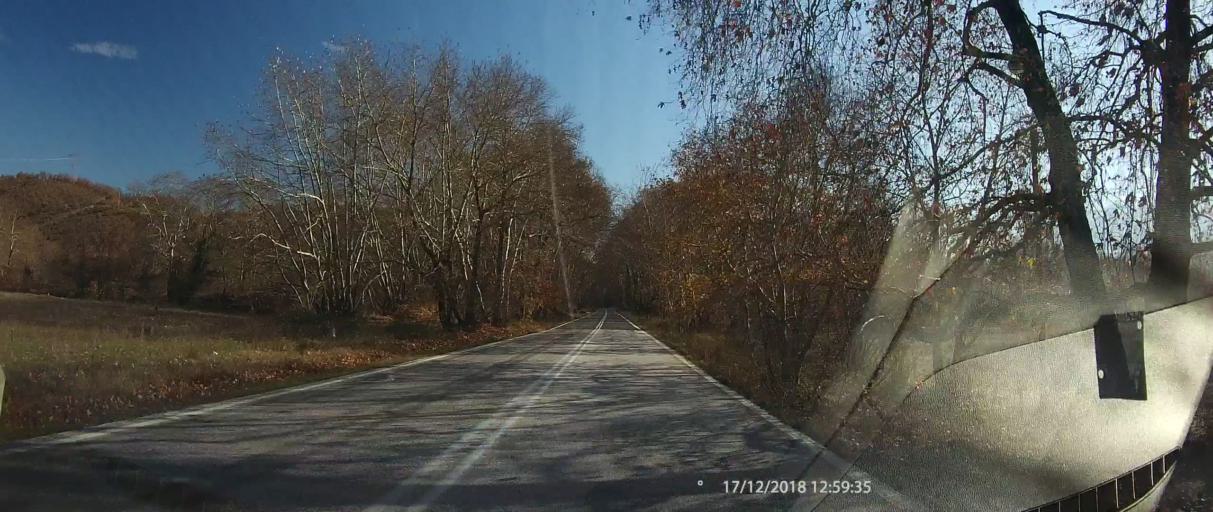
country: GR
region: Thessaly
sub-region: Trikala
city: Kastraki
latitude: 39.7361
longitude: 21.5576
